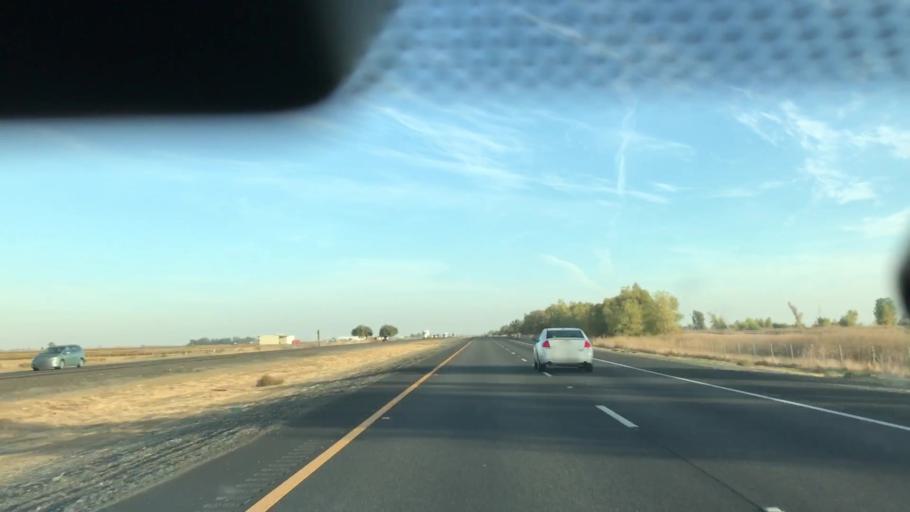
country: US
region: California
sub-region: Glenn County
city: Willows
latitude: 39.4301
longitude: -122.1932
